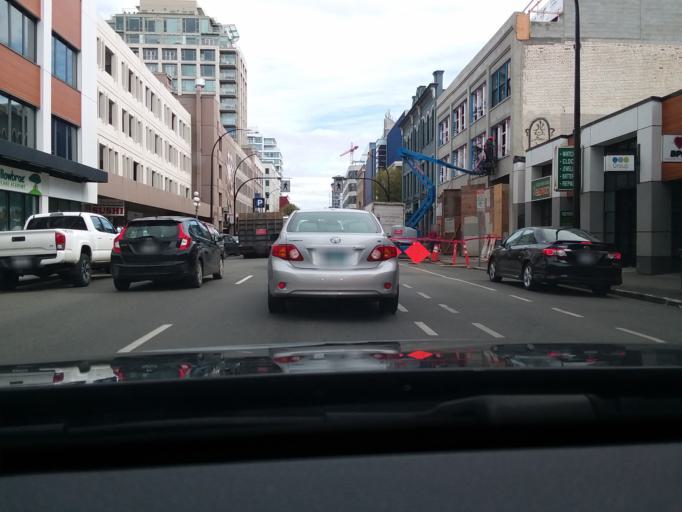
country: CA
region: British Columbia
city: Victoria
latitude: 48.4271
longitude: -123.3639
